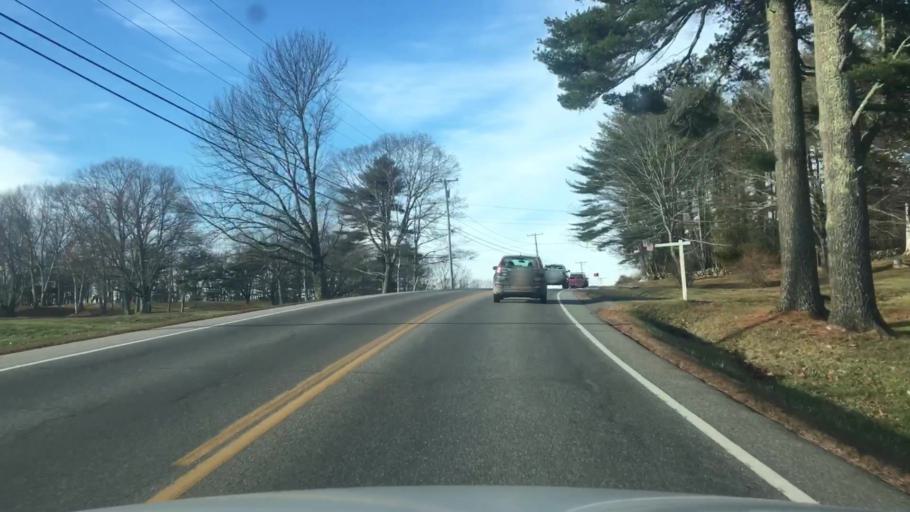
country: US
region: Maine
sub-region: Lincoln County
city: Edgecomb
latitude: 43.9336
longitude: -69.6207
